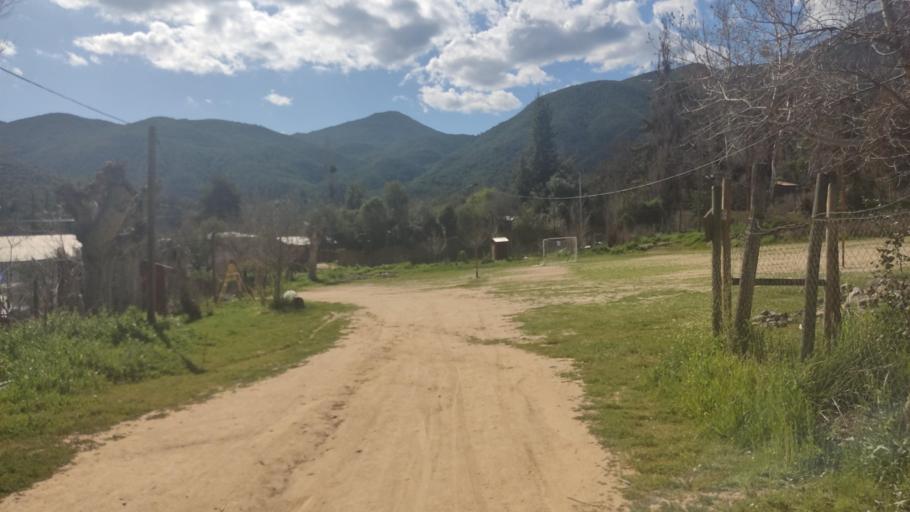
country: CL
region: Valparaiso
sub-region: Provincia de Marga Marga
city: Limache
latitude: -33.1732
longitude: -71.1650
